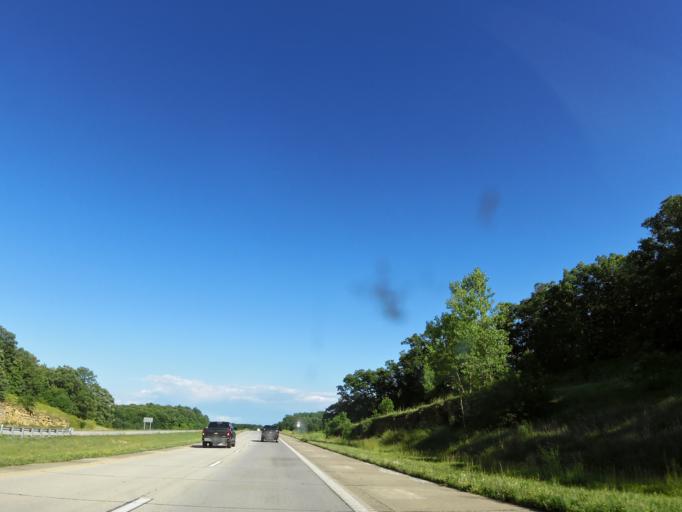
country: US
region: Missouri
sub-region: Pike County
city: Bowling Green
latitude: 39.3552
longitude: -91.1980
